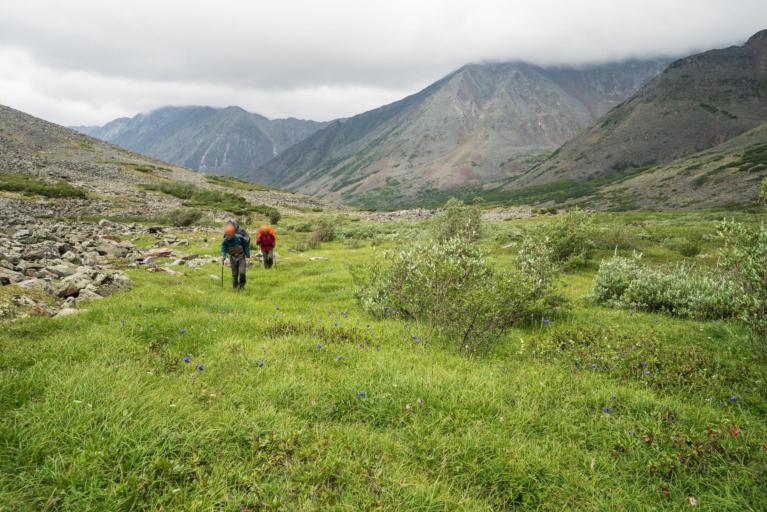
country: RU
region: Transbaikal Territory
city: Kuanda
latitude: 56.7592
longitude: 116.5473
